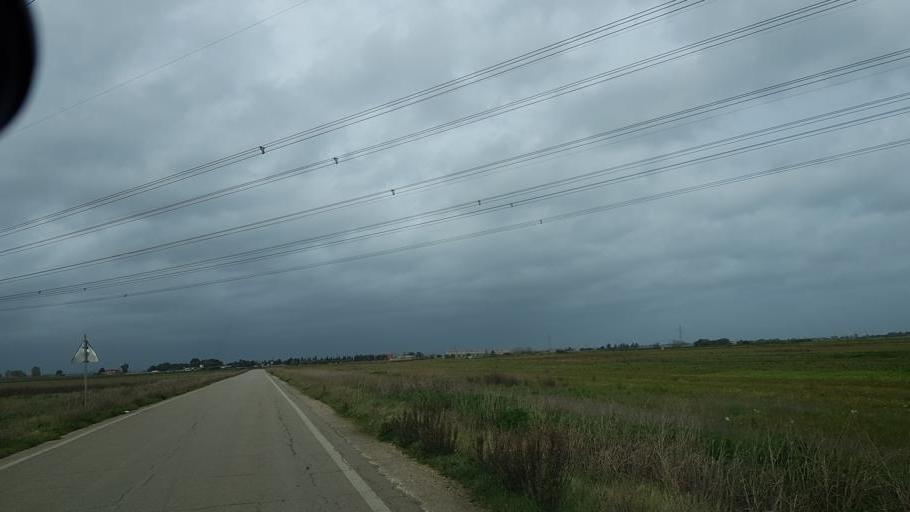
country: IT
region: Apulia
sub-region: Provincia di Brindisi
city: Brindisi
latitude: 40.6001
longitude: 17.8963
